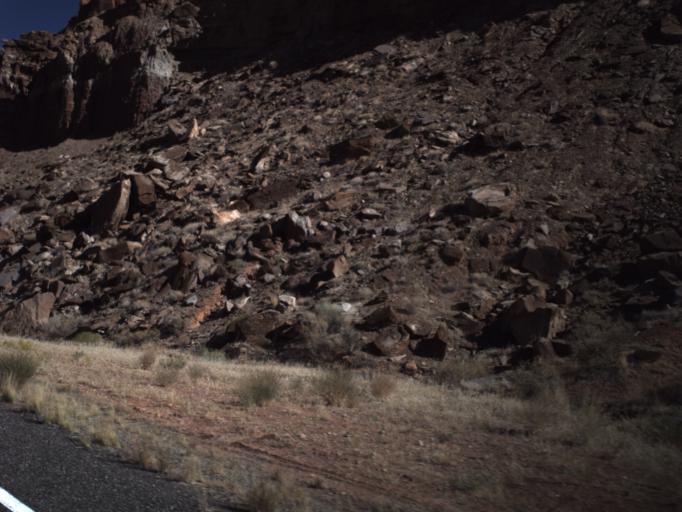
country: US
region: Utah
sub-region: San Juan County
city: Blanding
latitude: 37.9140
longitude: -110.4595
